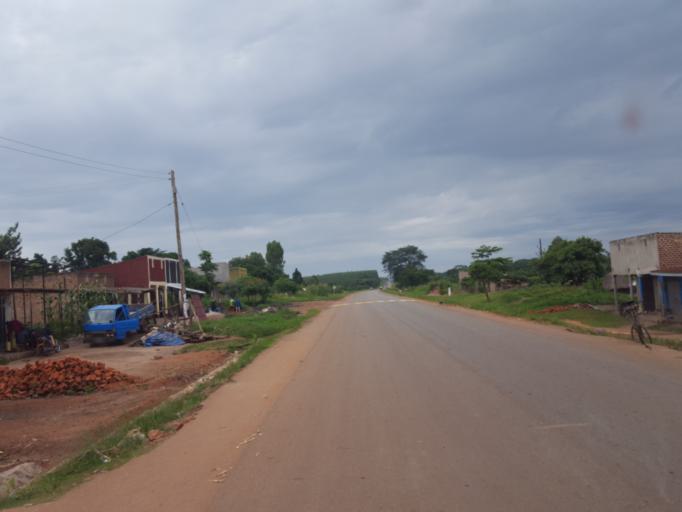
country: UG
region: Central Region
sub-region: Kiboga District
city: Kiboga
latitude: 1.0663
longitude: 31.6540
